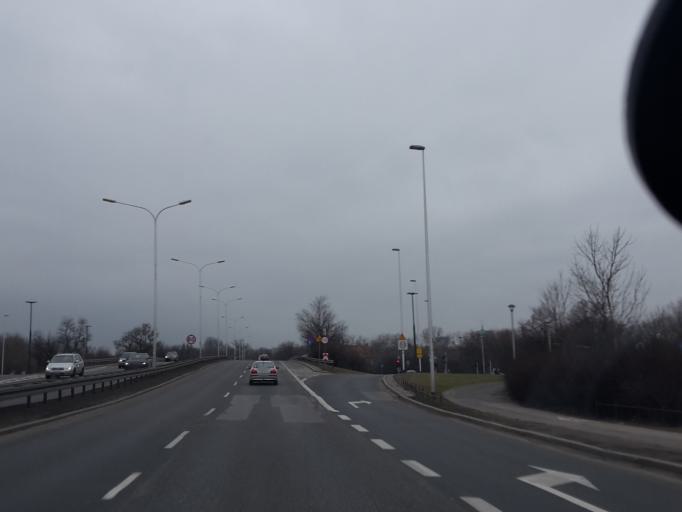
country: PL
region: Masovian Voivodeship
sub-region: Warszawa
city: Zoliborz
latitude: 52.2742
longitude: 20.9954
